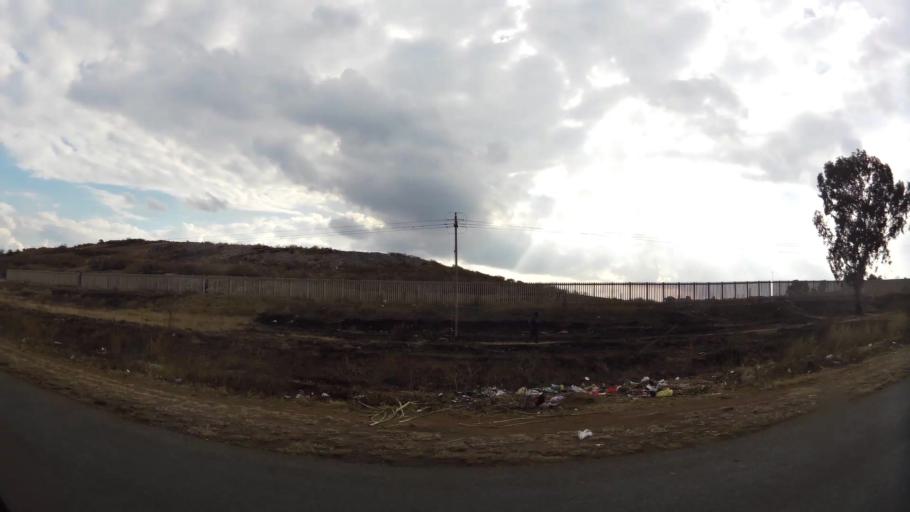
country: ZA
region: Gauteng
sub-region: Sedibeng District Municipality
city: Vanderbijlpark
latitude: -26.6680
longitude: 27.8631
